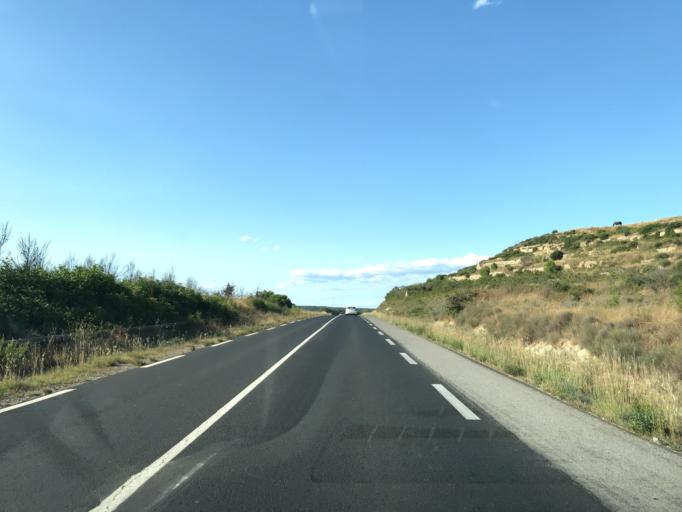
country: FR
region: Languedoc-Roussillon
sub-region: Departement de l'Herault
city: Montbazin
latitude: 43.5048
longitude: 3.6840
